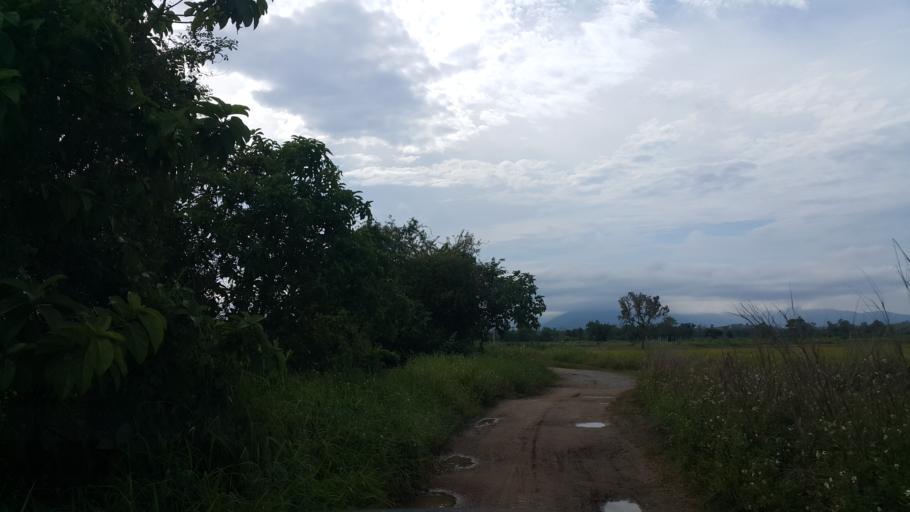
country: TH
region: Chiang Rai
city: Wiang Chai
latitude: 19.9722
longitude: 99.9177
